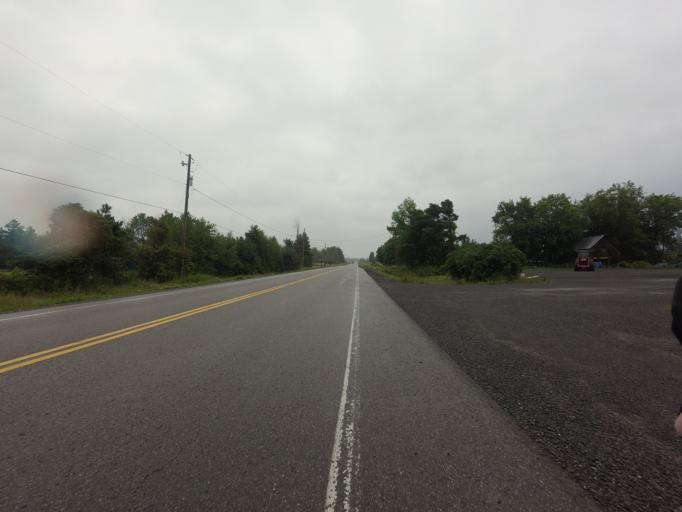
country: CA
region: Ontario
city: Perth
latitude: 45.0992
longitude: -76.3936
